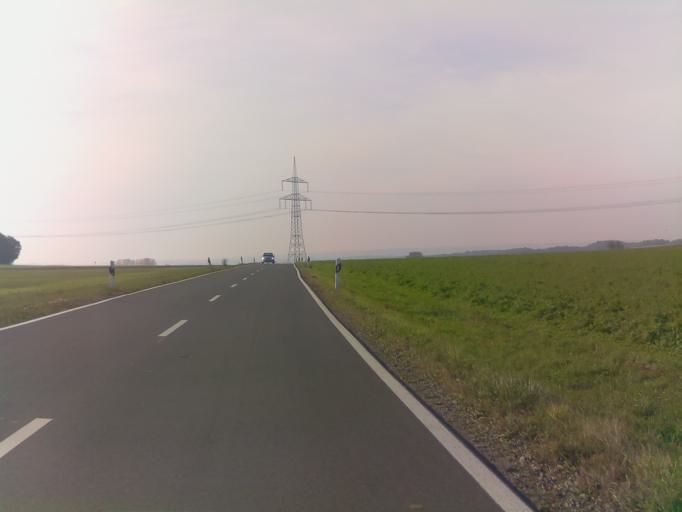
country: DE
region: Bavaria
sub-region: Regierungsbezirk Unterfranken
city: Theilheim
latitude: 49.7369
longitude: 10.0585
